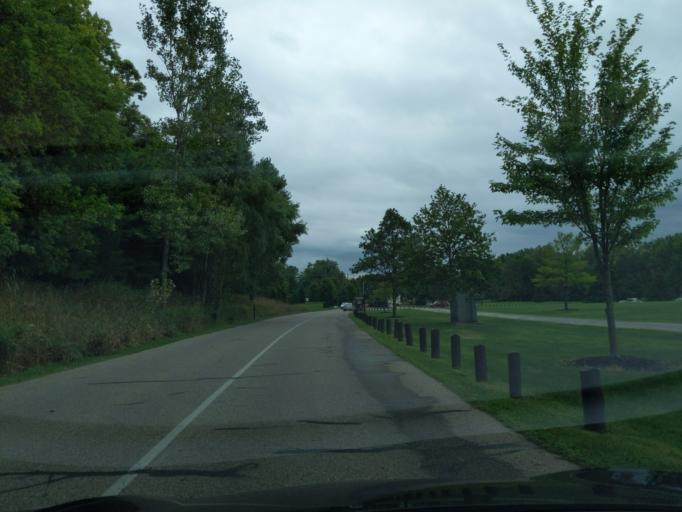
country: US
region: Michigan
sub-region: Ingham County
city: Lansing
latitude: 42.6925
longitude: -84.5285
